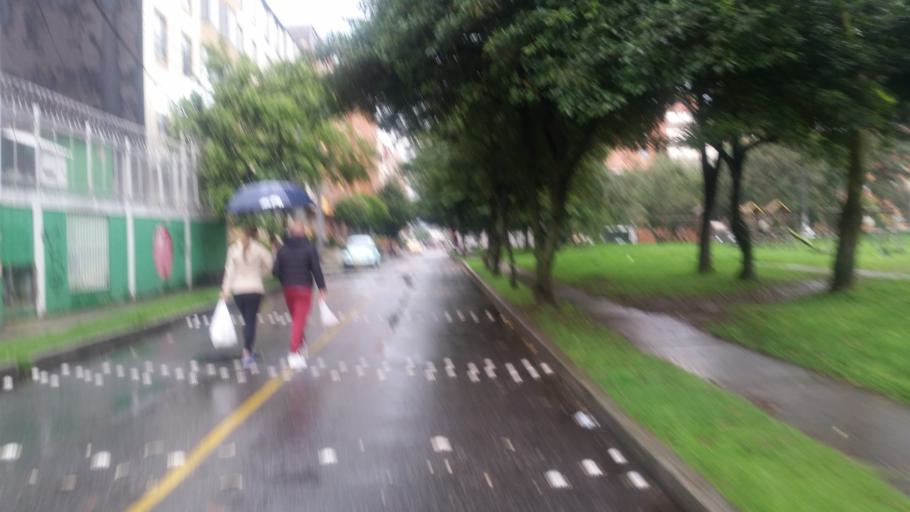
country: CO
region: Bogota D.C.
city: Bogota
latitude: 4.6344
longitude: -74.0982
